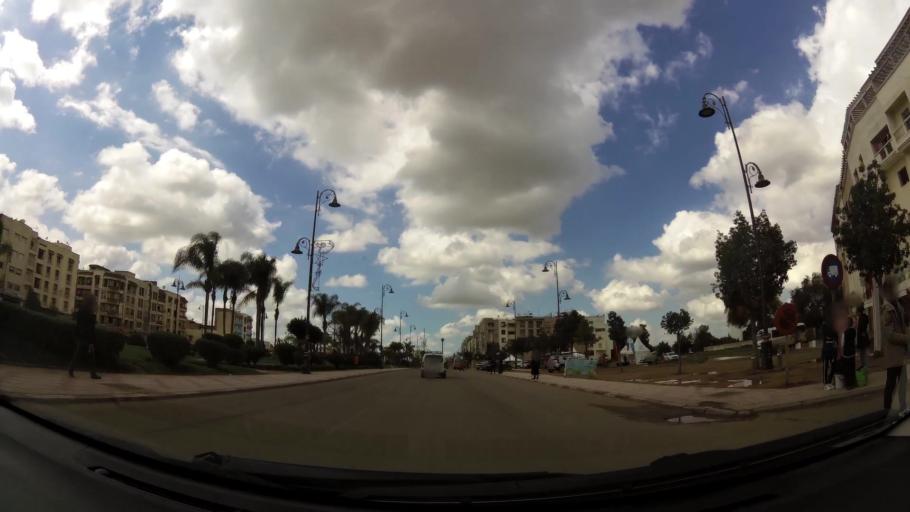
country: MA
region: Chaouia-Ouardigha
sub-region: Settat Province
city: Berrechid
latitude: 33.2677
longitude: -7.5836
